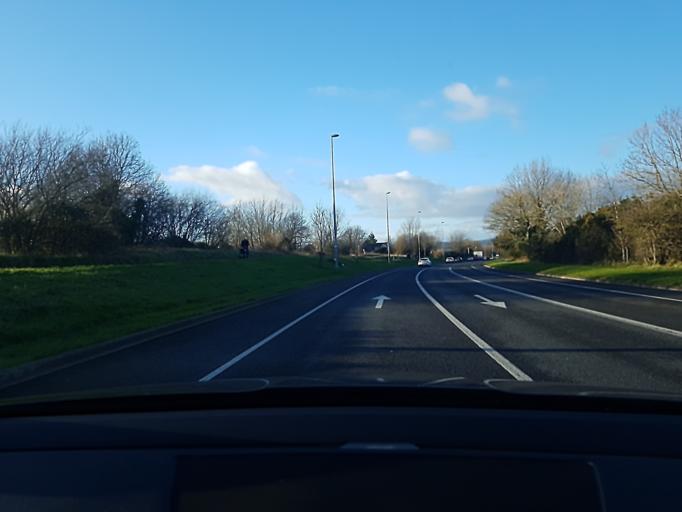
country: IE
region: Munster
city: Moyross
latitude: 52.6620
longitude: -8.6662
